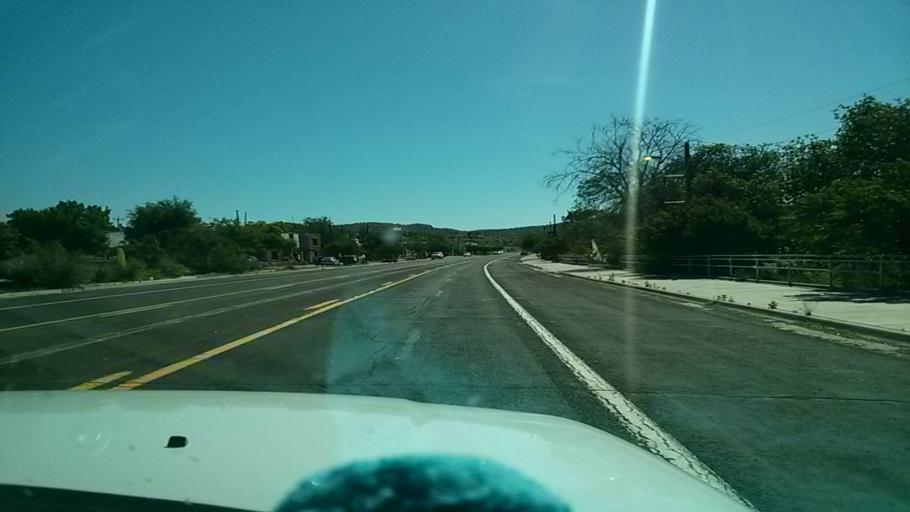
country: US
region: Arizona
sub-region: Mohave County
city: Peach Springs
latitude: 35.5284
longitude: -113.4287
